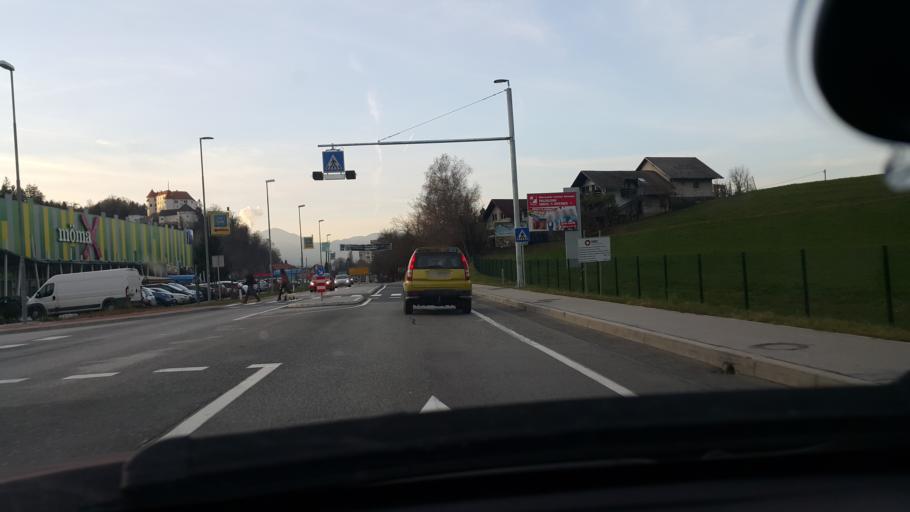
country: SI
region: Velenje
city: Velenje
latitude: 46.3553
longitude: 15.1179
